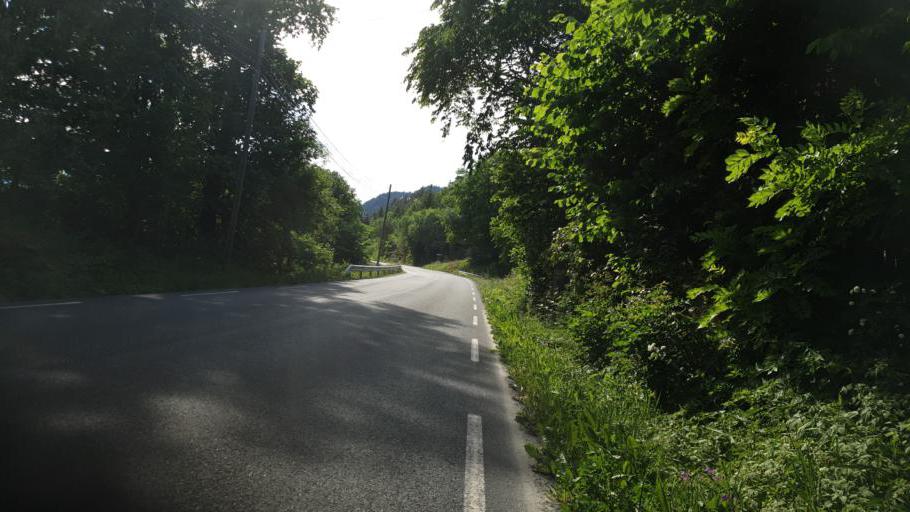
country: NO
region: Sor-Trondelag
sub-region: Trondheim
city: Trondheim
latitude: 63.5571
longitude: 10.2993
